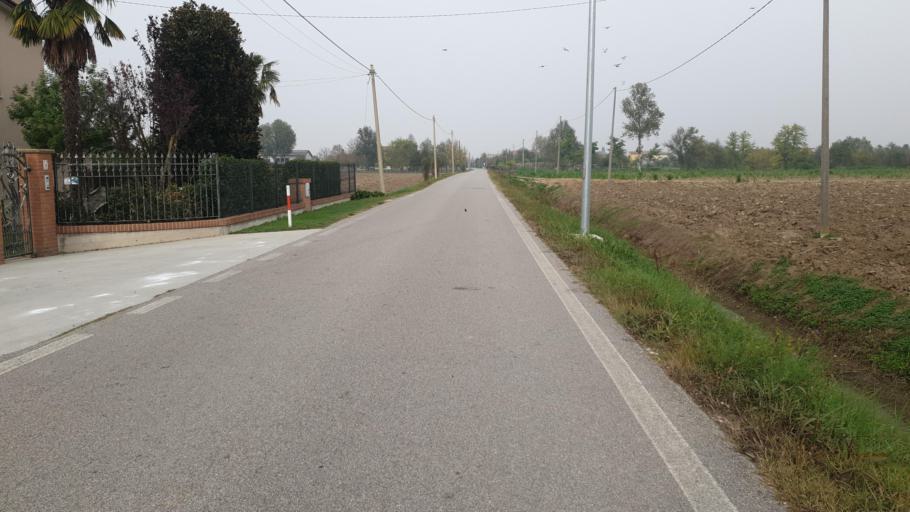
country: IT
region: Veneto
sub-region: Provincia di Padova
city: Casalserugo
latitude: 45.2884
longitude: 11.9071
